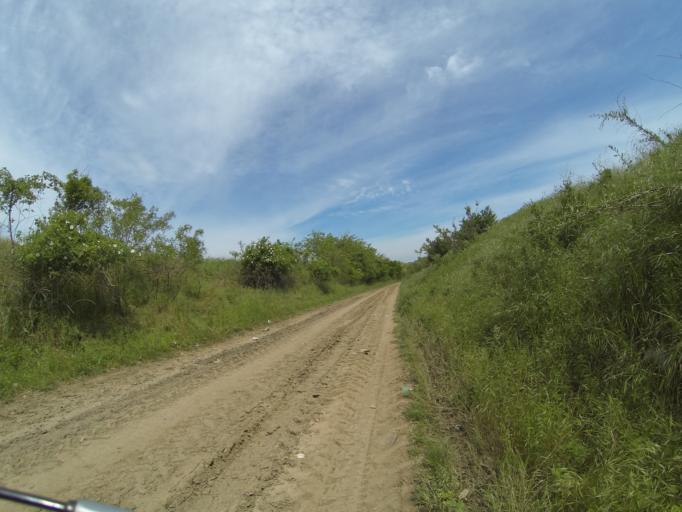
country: RO
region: Dolj
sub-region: Comuna Leu
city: Leu
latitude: 44.1983
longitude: 23.9922
